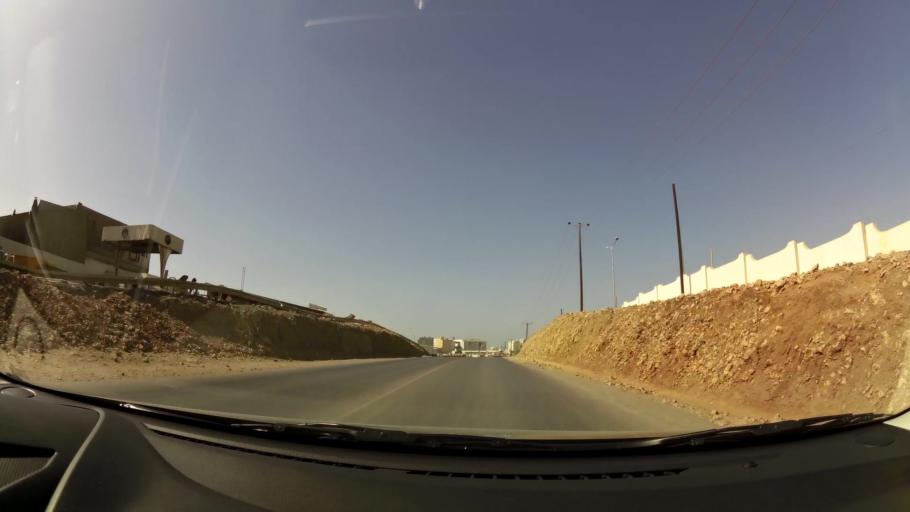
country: OM
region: Muhafazat Masqat
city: Bawshar
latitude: 23.5782
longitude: 58.3619
